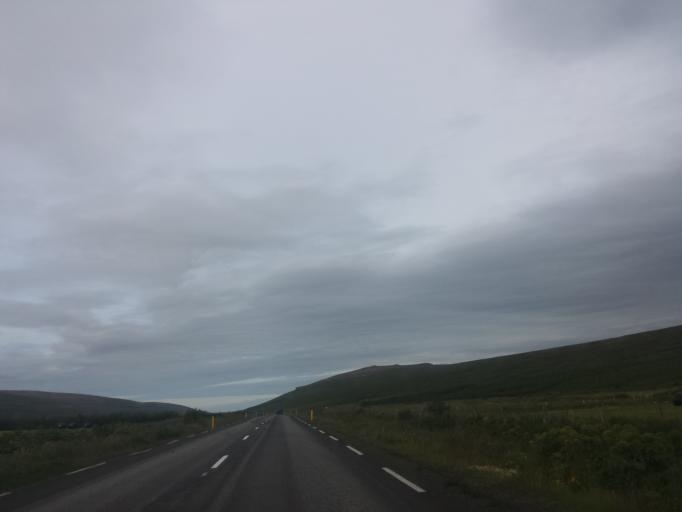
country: IS
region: Northeast
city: Laugar
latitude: 65.7514
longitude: -17.5874
